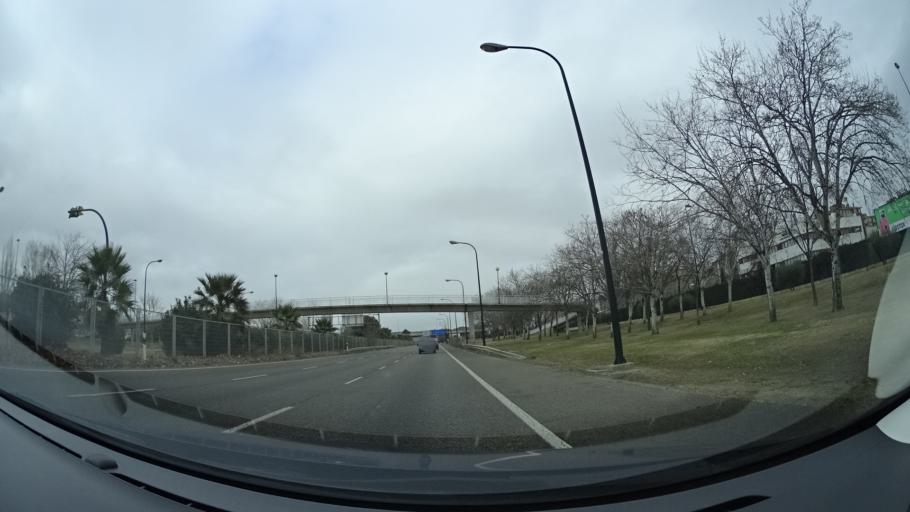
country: ES
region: Aragon
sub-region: Provincia de Zaragoza
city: Zaragoza
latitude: 41.6700
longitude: -0.8801
